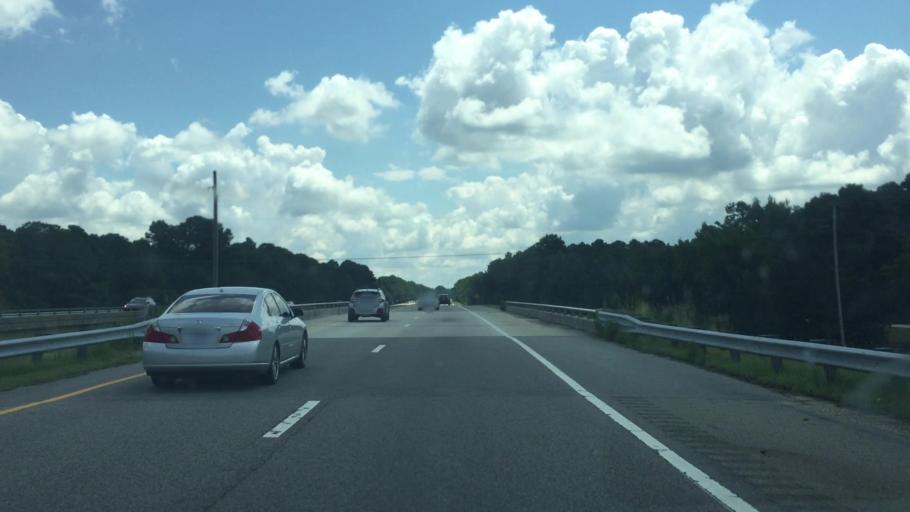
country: US
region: North Carolina
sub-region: Robeson County
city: Lumberton
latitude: 34.5799
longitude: -79.0488
